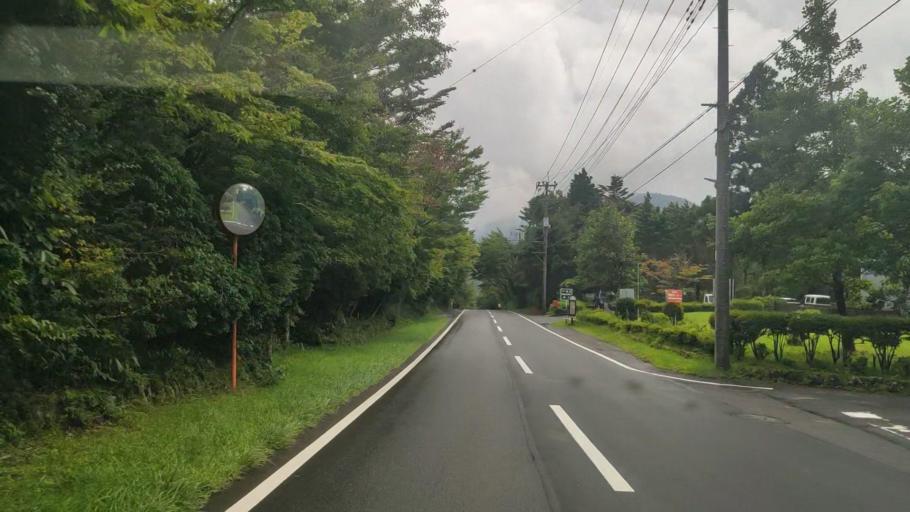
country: JP
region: Shizuoka
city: Gotemba
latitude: 35.2653
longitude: 138.8062
